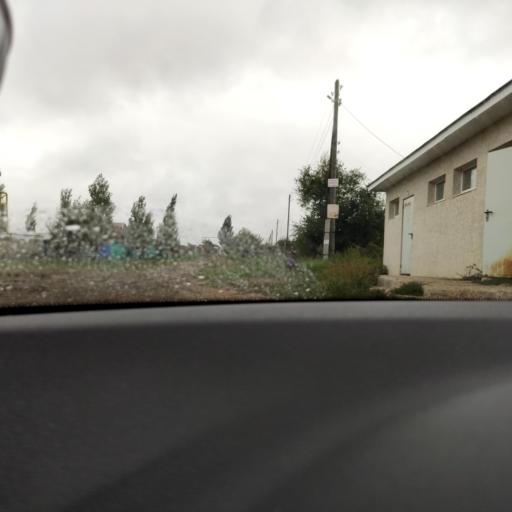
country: RU
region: Samara
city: Yelkhovka
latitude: 53.7446
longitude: 50.2592
